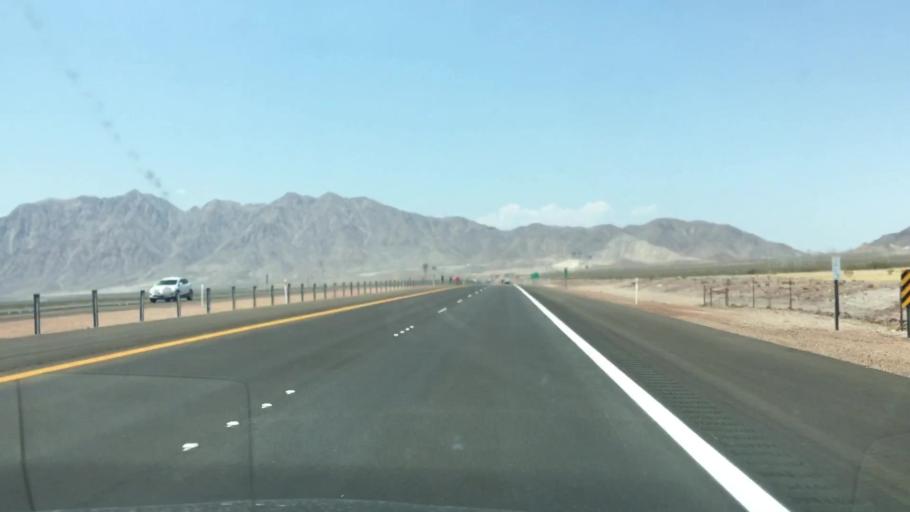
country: US
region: Nevada
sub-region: Clark County
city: Boulder City
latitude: 35.9402
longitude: -114.8755
